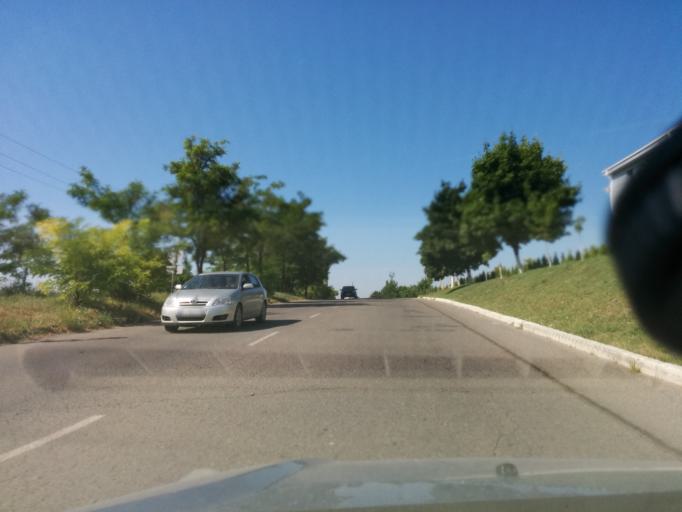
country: MD
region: Chisinau
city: Chisinau
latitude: 47.0433
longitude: 28.9069
